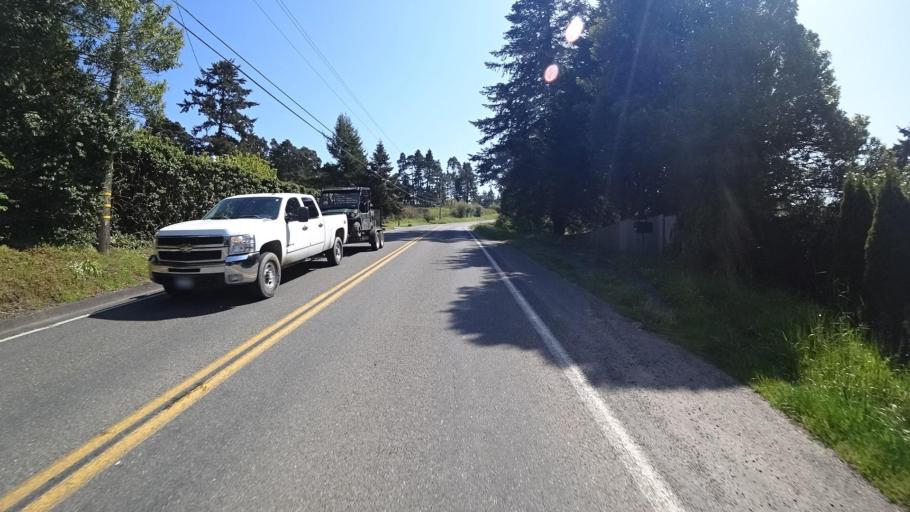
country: US
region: California
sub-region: Humboldt County
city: Hydesville
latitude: 40.5532
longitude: -124.1046
